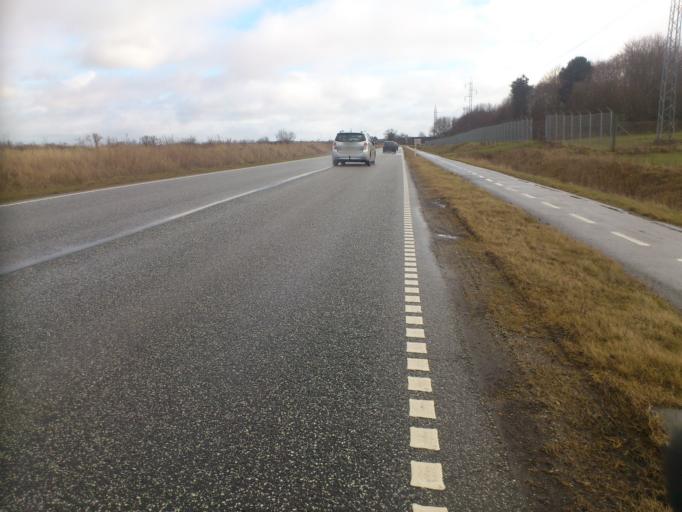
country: DK
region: South Denmark
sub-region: Fredericia Kommune
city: Fredericia
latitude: 55.6003
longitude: 9.7513
